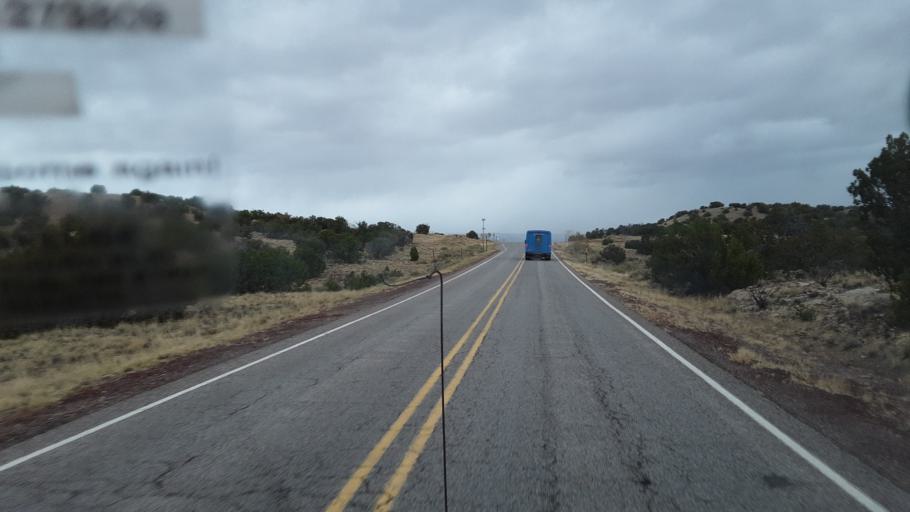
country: US
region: New Mexico
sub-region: Rio Arriba County
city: Santa Teresa
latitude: 36.2519
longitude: -106.4079
